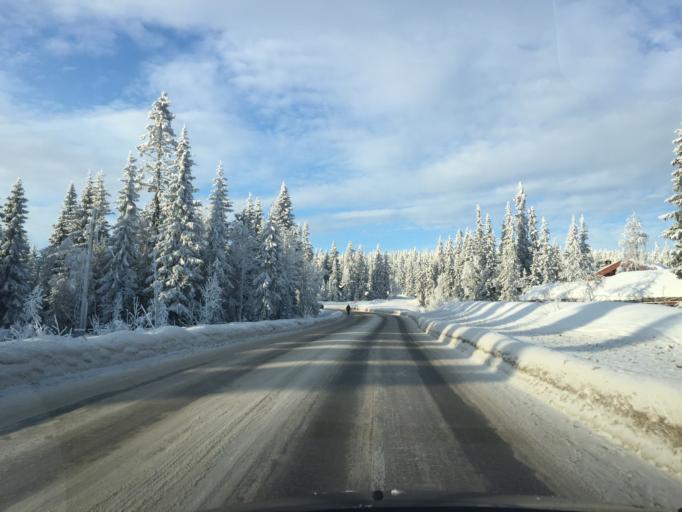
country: NO
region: Hedmark
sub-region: Trysil
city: Innbygda
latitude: 61.3337
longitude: 12.1685
